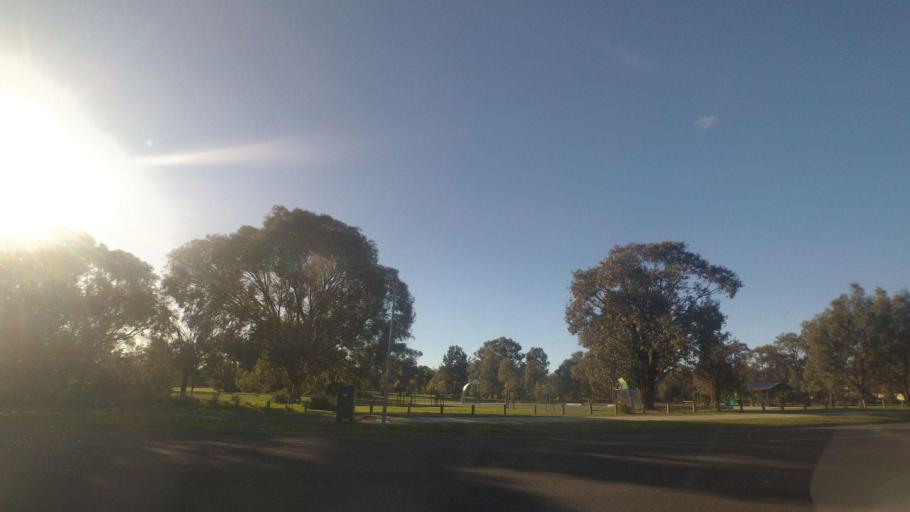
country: AU
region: Victoria
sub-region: Knox
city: Rowville
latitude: -37.9269
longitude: 145.2587
